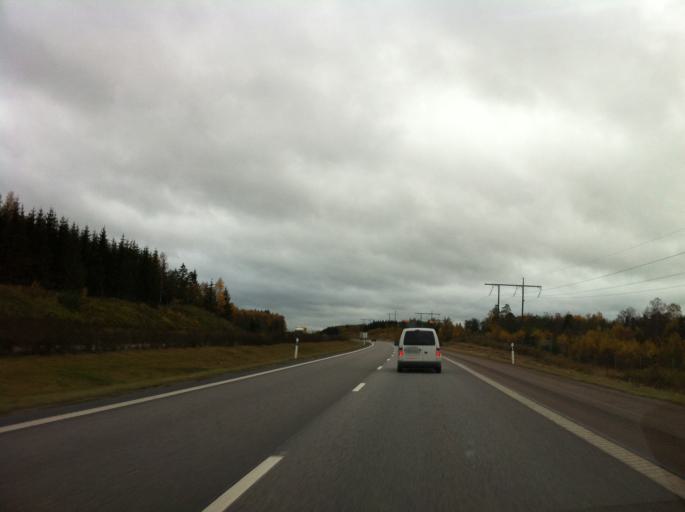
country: SE
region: OEstergoetland
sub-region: Vadstena Kommun
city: Herrestad
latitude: 58.2822
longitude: 14.8710
